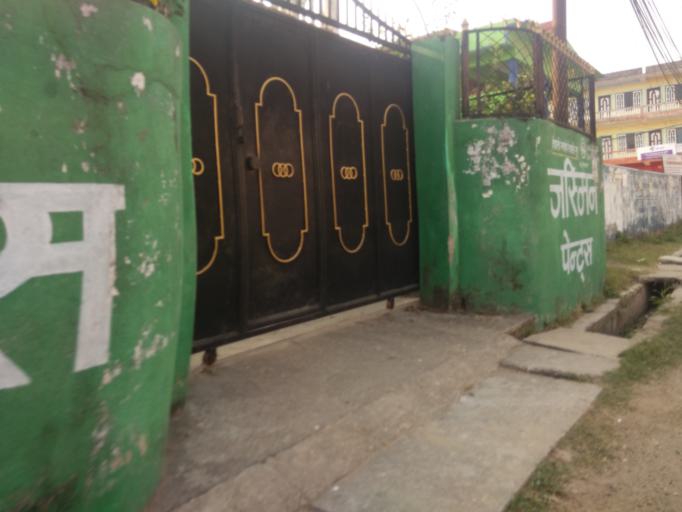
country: NP
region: Central Region
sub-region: Narayani Zone
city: Hitura
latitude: 27.4328
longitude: 85.0361
